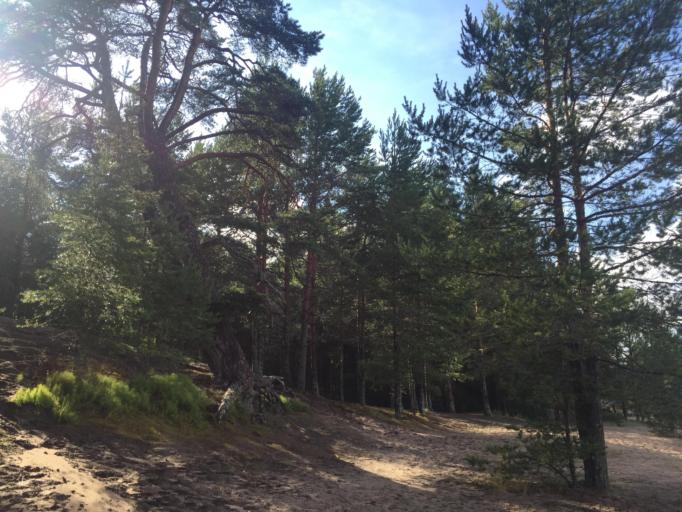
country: RU
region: Leningrad
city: Priozersk
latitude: 60.9772
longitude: 30.2893
